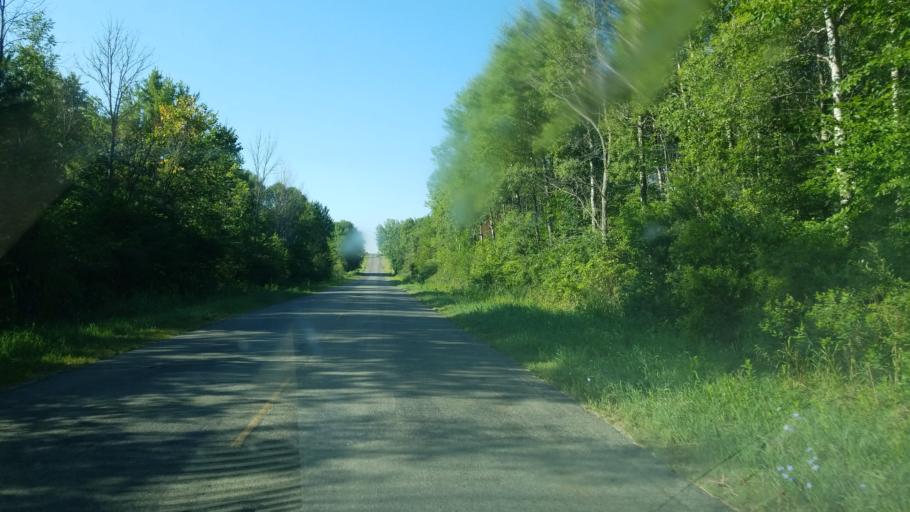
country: US
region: Michigan
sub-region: Mecosta County
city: Canadian Lakes
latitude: 43.5002
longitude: -85.3929
